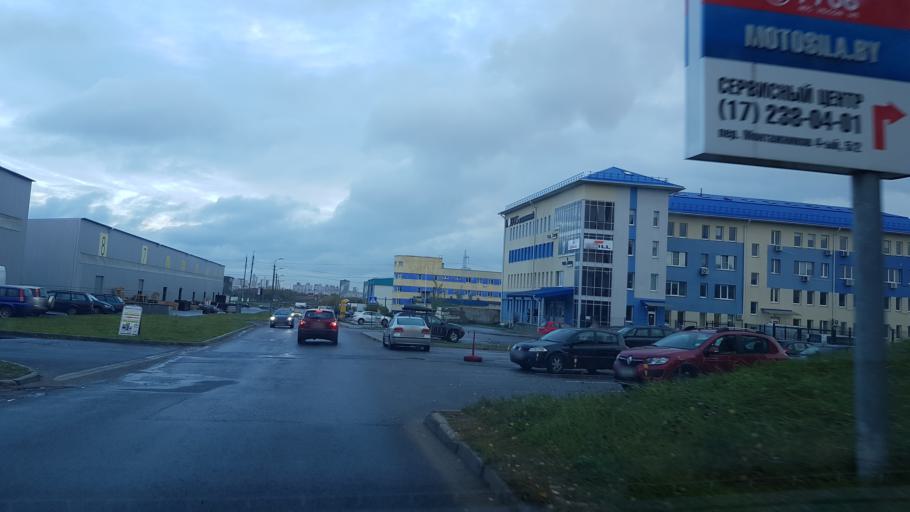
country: BY
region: Minsk
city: Malinovka
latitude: 53.8765
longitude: 27.4123
